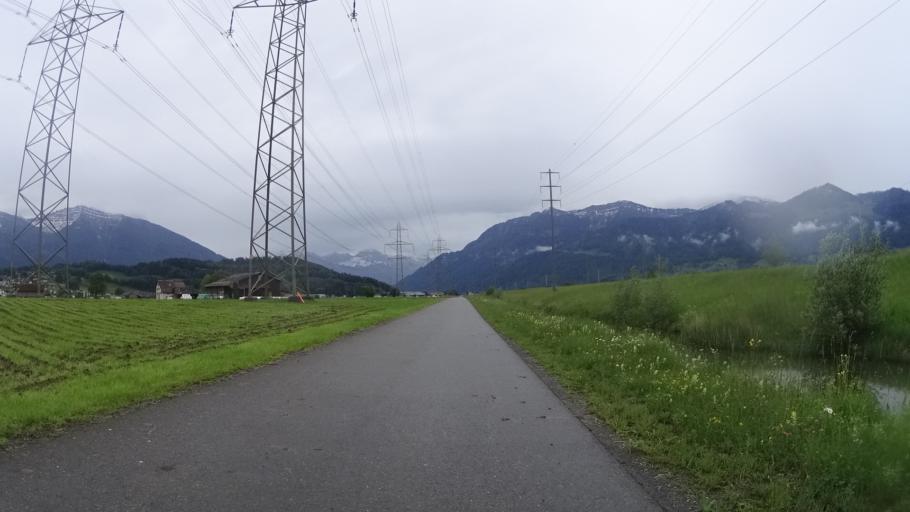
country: CH
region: Saint Gallen
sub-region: Wahlkreis See-Gaster
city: Benken
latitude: 47.2020
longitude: 8.9828
